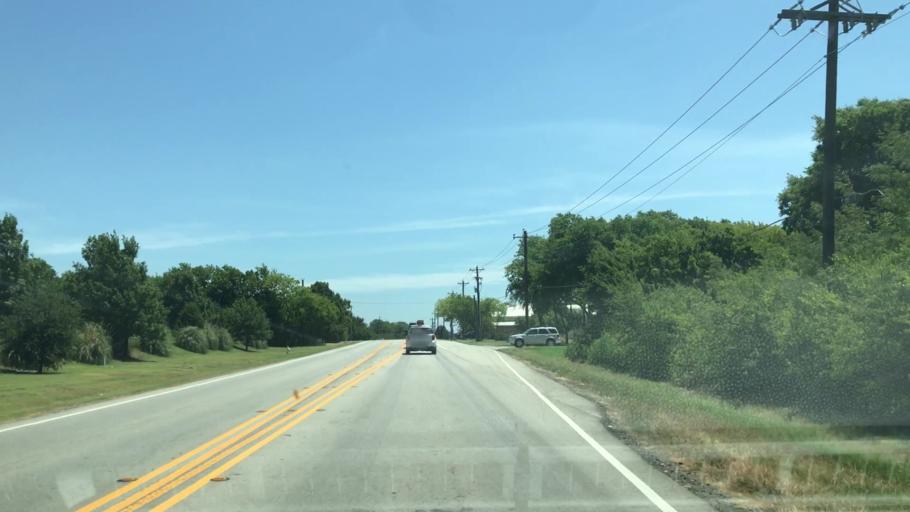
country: US
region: Texas
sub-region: Collin County
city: Lucas
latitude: 33.0852
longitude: -96.5843
